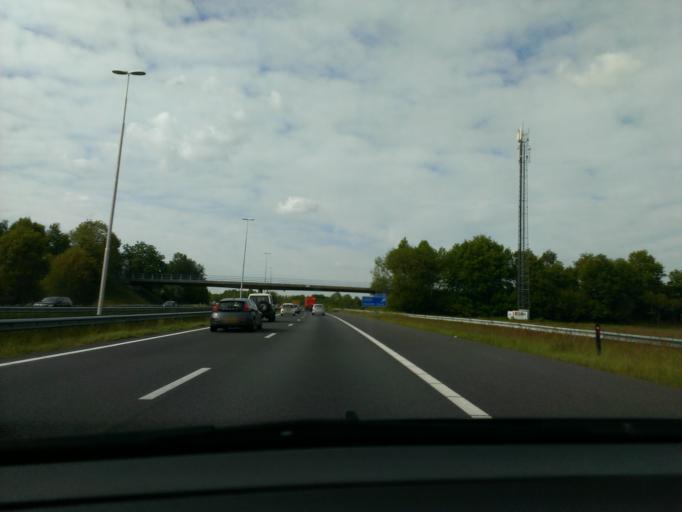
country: NL
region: Gelderland
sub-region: Gemeente Epe
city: Oene
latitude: 52.3608
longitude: 6.0260
